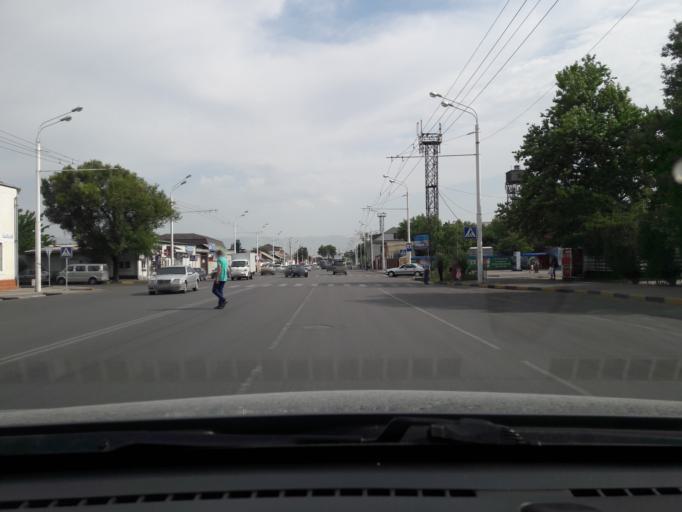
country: TJ
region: Dushanbe
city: Dushanbe
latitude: 38.5437
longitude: 68.7553
